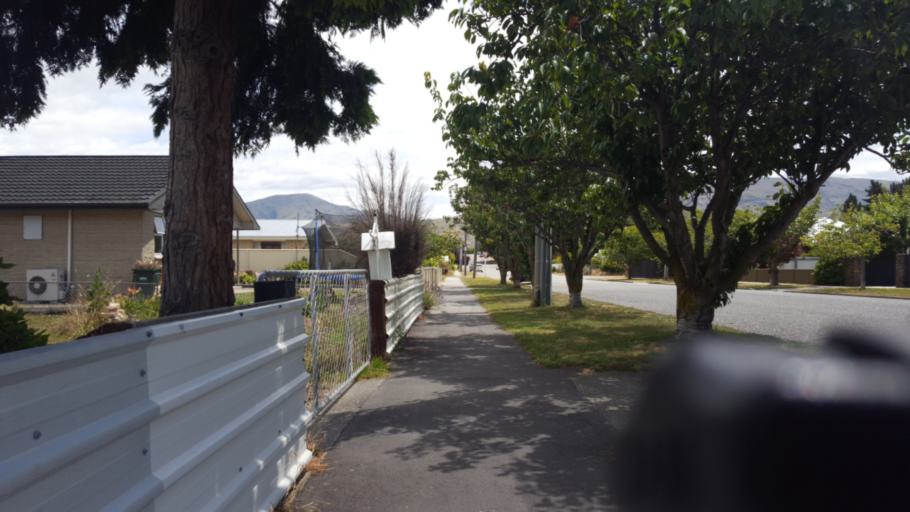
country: NZ
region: Otago
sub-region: Queenstown-Lakes District
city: Wanaka
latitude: -45.0446
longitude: 169.2103
